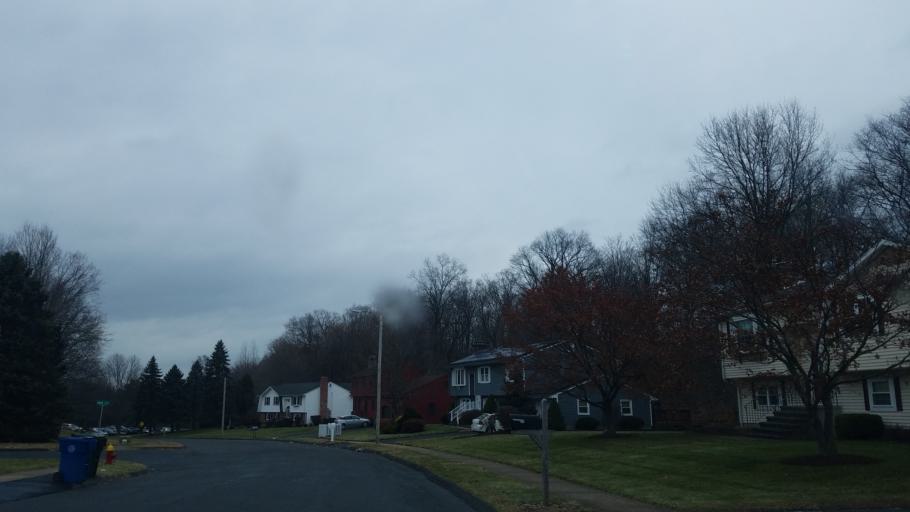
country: US
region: Connecticut
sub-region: Hartford County
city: Kensington
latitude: 41.6250
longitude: -72.7749
